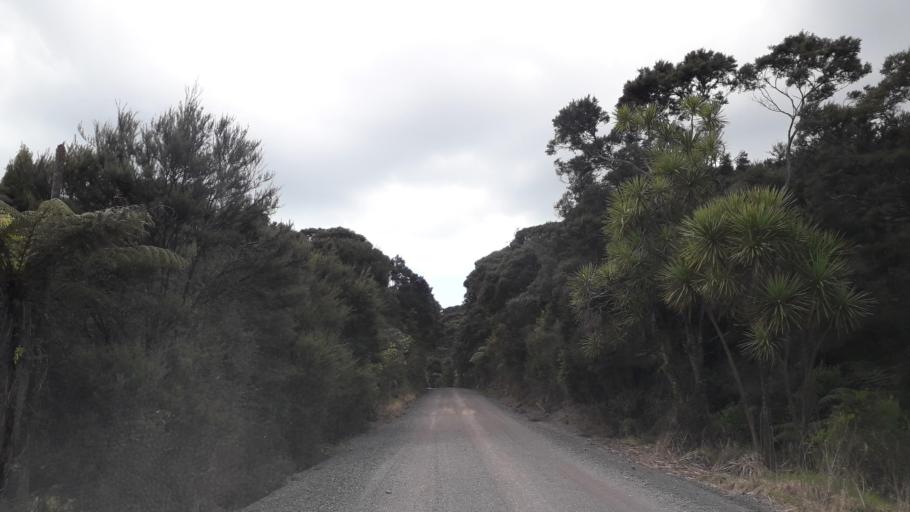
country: NZ
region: Northland
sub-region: Far North District
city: Paihia
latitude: -35.3136
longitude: 174.2242
